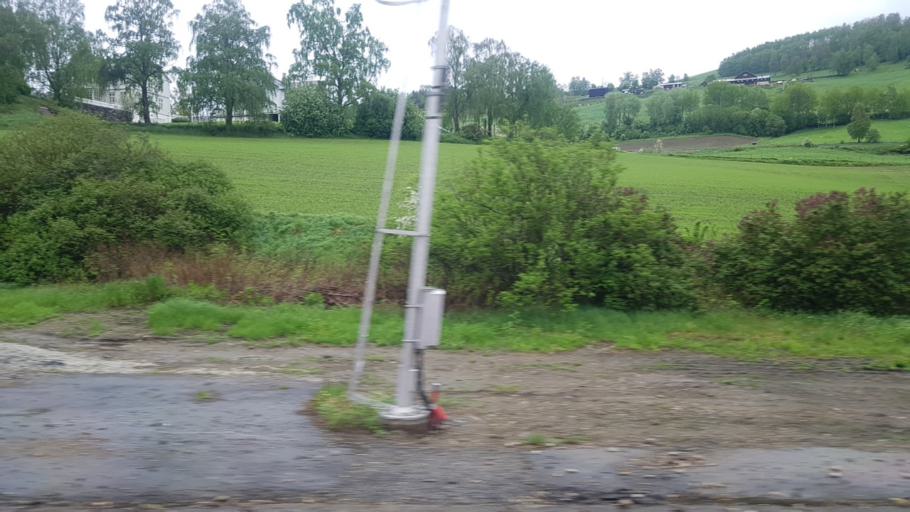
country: NO
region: Oppland
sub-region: Sor-Fron
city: Hundorp
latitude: 61.5643
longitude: 9.9273
